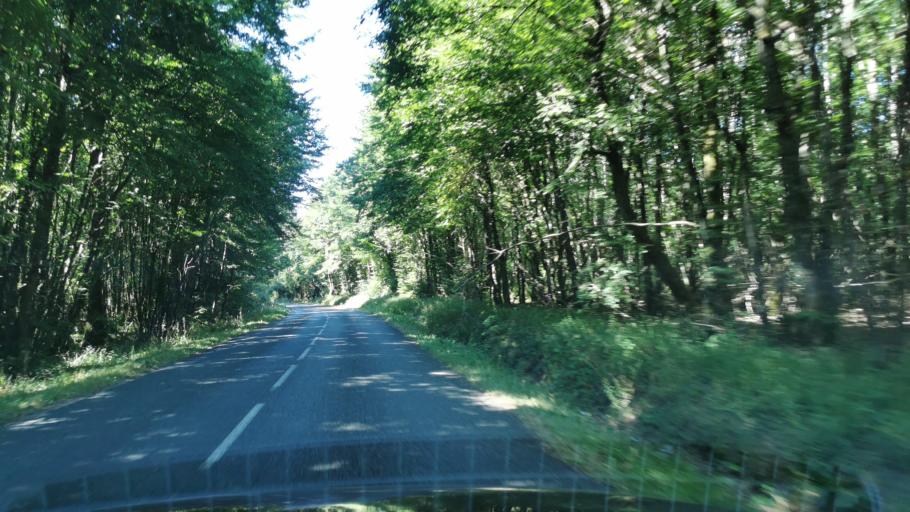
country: FR
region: Bourgogne
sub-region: Departement de Saone-et-Loire
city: Torcy
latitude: 46.7747
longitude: 4.4724
